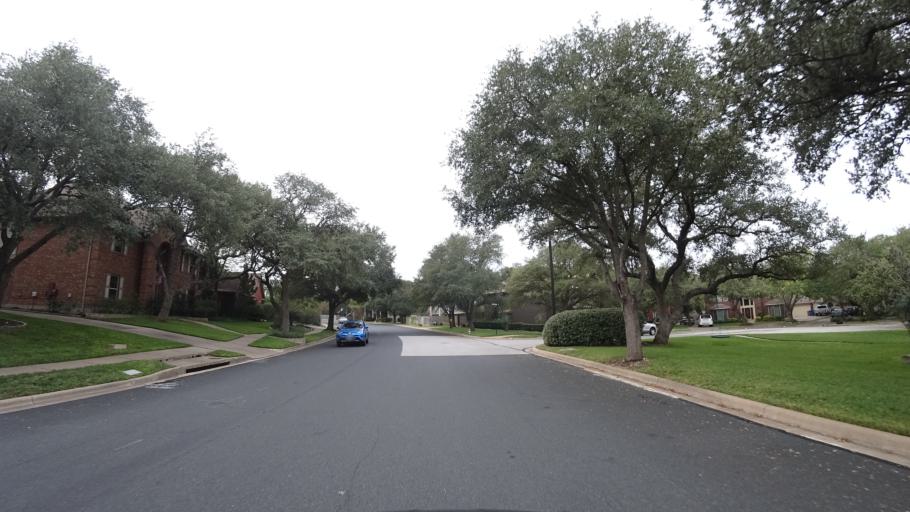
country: US
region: Texas
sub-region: Travis County
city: Shady Hollow
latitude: 30.1922
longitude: -97.8940
